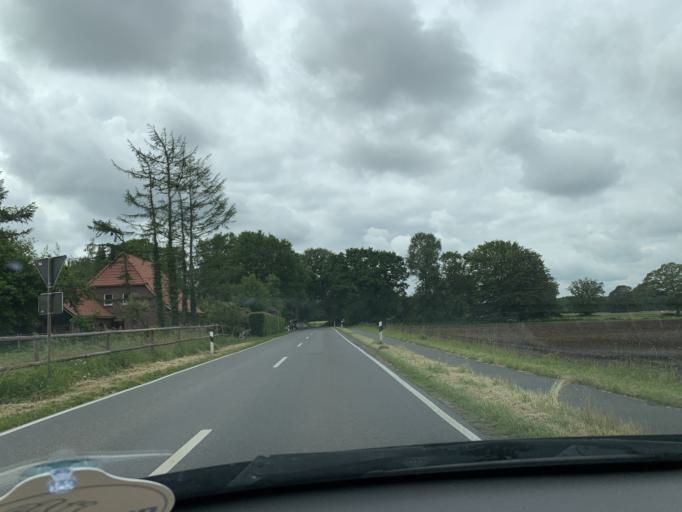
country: DE
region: Lower Saxony
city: Bockhorn
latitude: 53.3837
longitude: 8.0562
